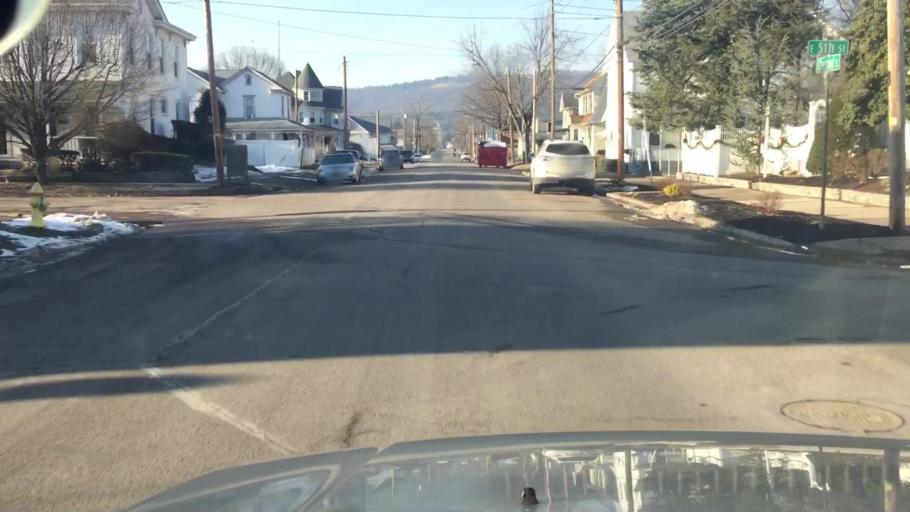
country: US
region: Pennsylvania
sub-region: Columbia County
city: Berwick
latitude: 41.0591
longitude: -76.2323
